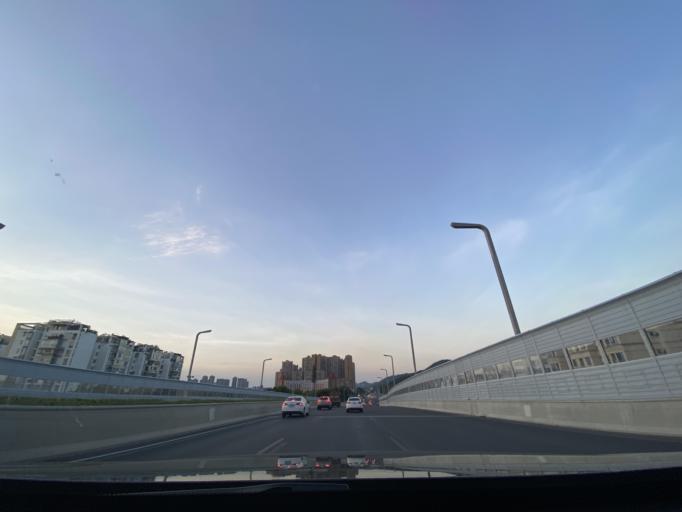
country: CN
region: Sichuan
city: Longquan
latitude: 30.5982
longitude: 104.3076
